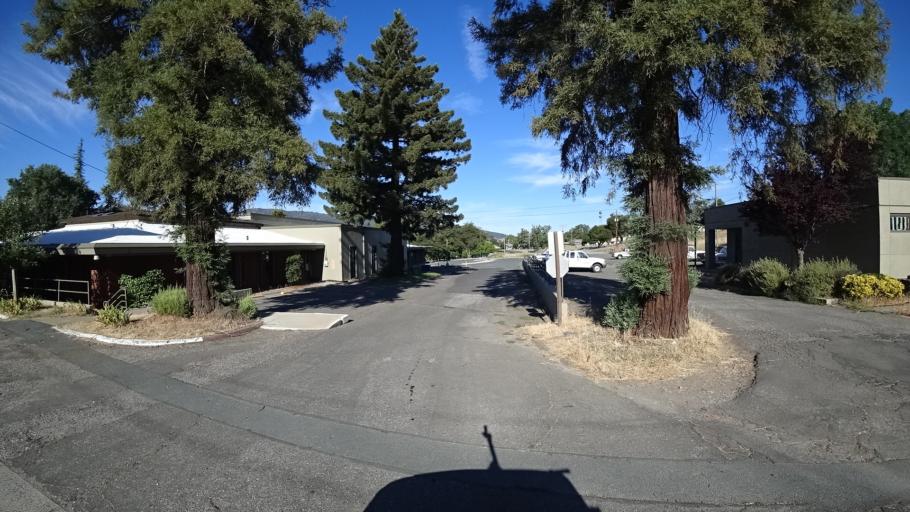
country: US
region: California
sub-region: Calaveras County
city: San Andreas
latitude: 38.1914
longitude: -120.6670
